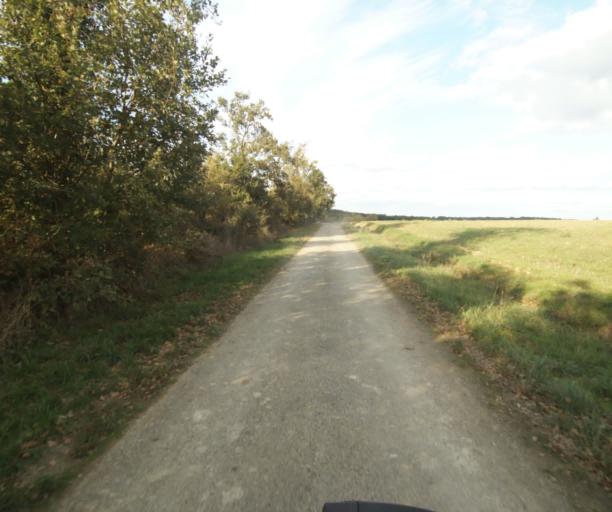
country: FR
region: Midi-Pyrenees
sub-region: Departement de la Haute-Garonne
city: Launac
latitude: 43.7992
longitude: 1.1158
